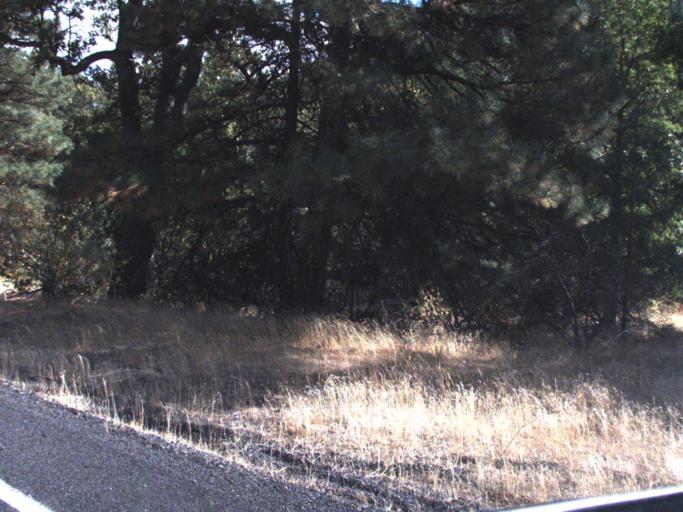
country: US
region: Washington
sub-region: Yakima County
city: Tieton
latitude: 46.7079
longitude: -120.8871
